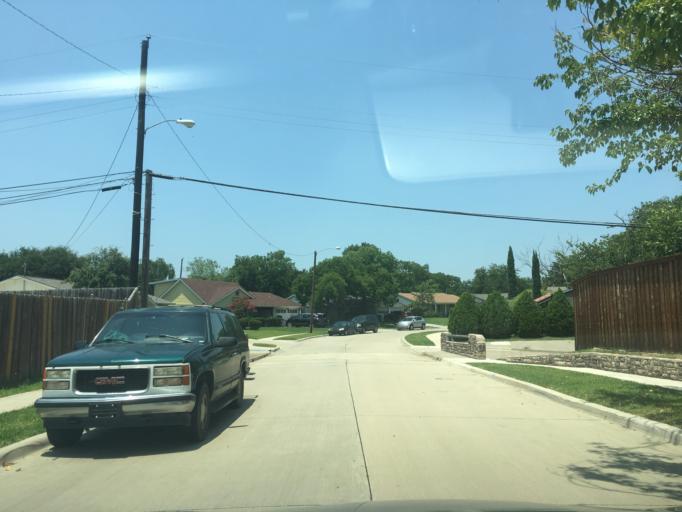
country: US
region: Texas
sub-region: Dallas County
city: Carrollton
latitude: 32.9483
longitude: -96.8760
